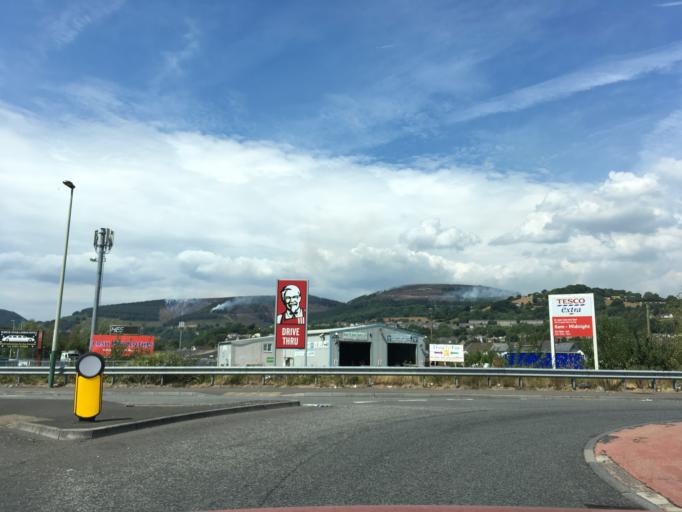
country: GB
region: Wales
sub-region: Caerphilly County Borough
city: Risca
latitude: 51.6015
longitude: -3.0932
